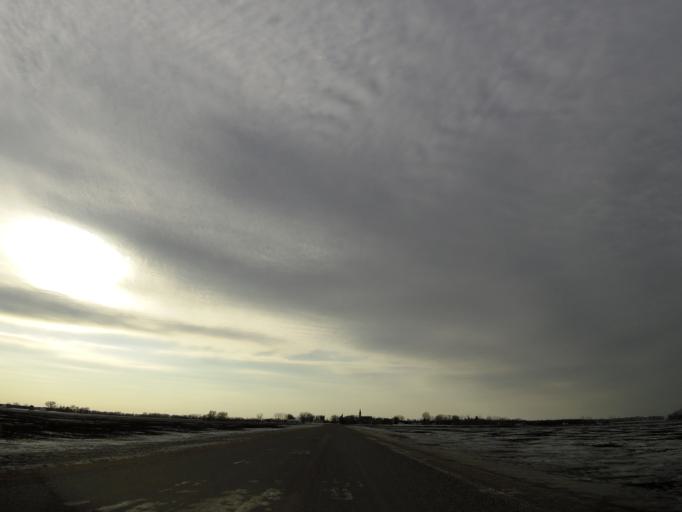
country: US
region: North Dakota
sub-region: Walsh County
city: Grafton
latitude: 48.4267
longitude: -97.2813
